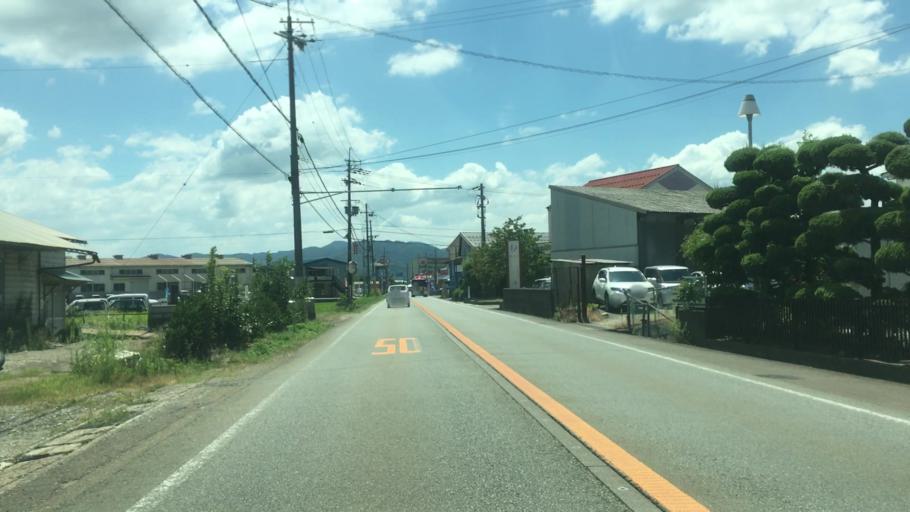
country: JP
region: Hyogo
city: Toyooka
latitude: 35.4989
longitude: 134.8052
